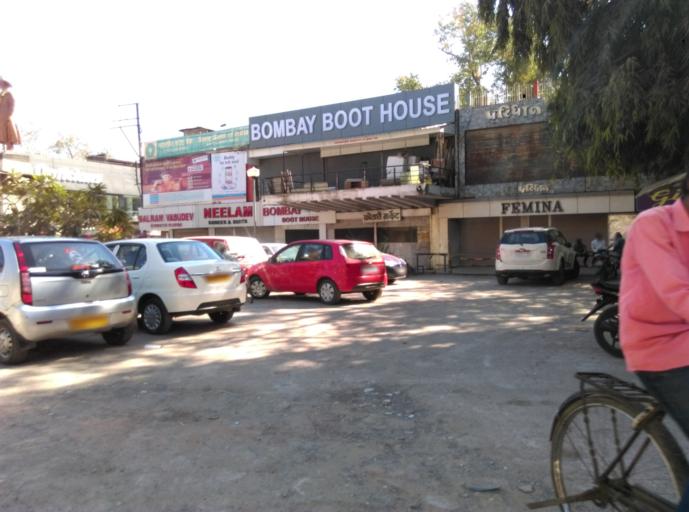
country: IN
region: Madhya Pradesh
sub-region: Indore
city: Indore
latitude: 22.7199
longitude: 75.8624
